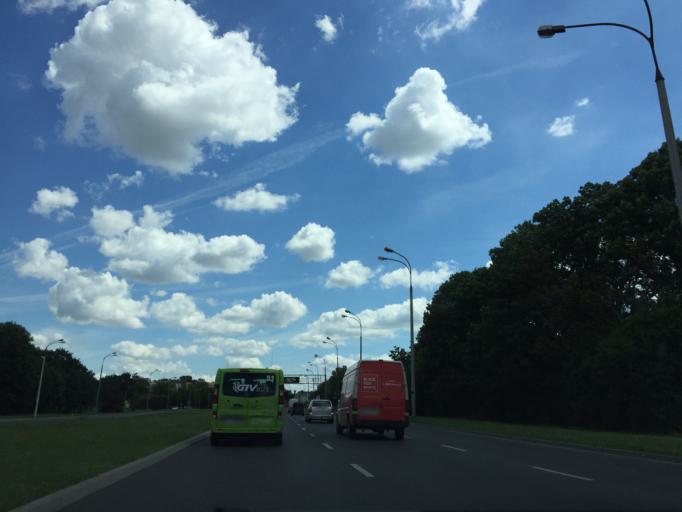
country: PL
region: Lublin Voivodeship
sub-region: Powiat lubelski
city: Lublin
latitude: 51.2532
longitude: 22.5561
